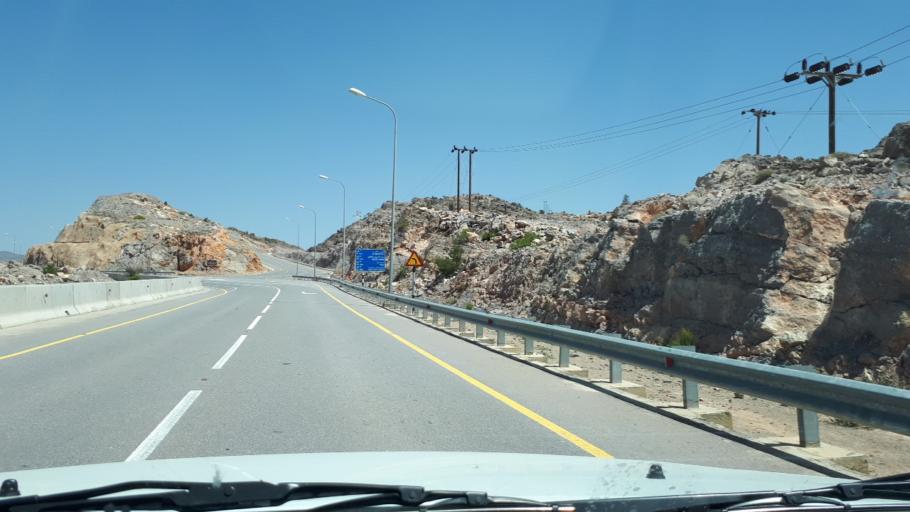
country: OM
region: Muhafazat ad Dakhiliyah
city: Izki
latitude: 23.0571
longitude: 57.7283
